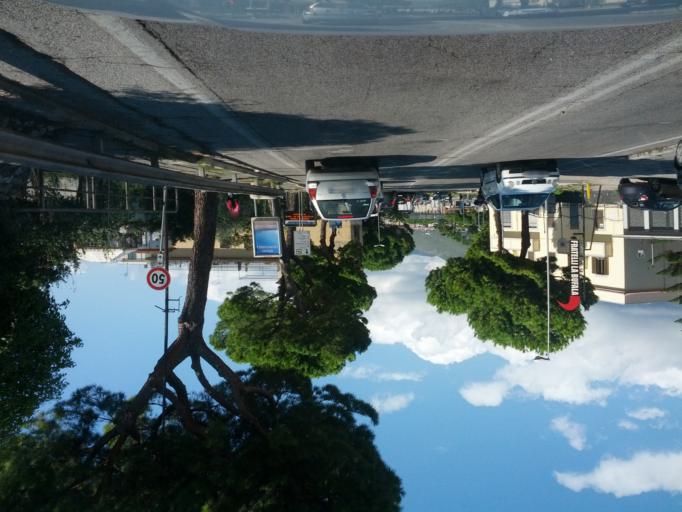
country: IT
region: Latium
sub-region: Provincia di Latina
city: Formia
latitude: 41.2539
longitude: 13.6052
